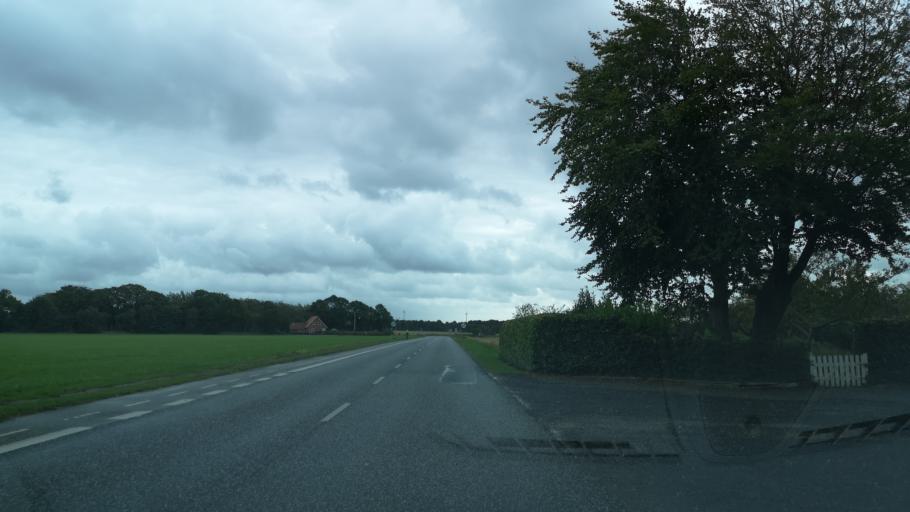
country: DK
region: Central Jutland
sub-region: Ringkobing-Skjern Kommune
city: Videbaek
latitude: 56.0455
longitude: 8.6840
